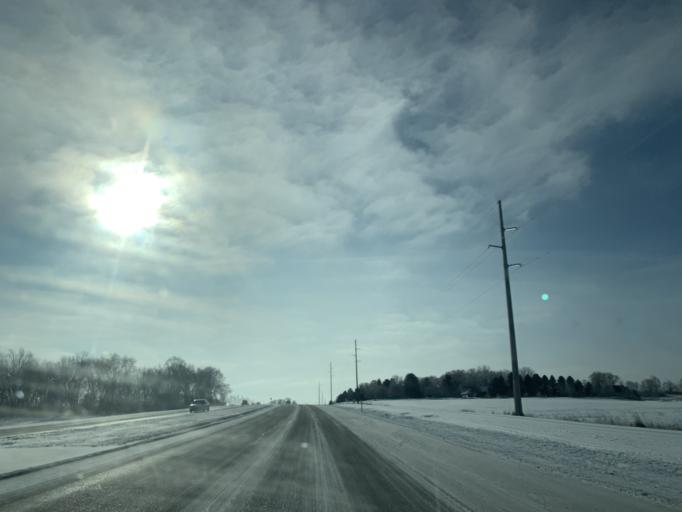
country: US
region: Minnesota
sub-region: Dakota County
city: Lakeville
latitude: 44.6801
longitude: -93.2173
